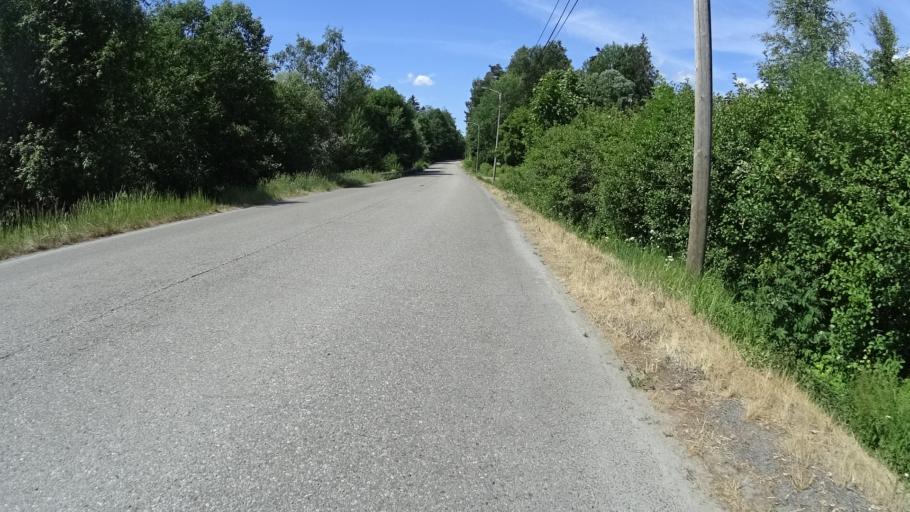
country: FI
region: Uusimaa
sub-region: Raaseporin
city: Karis
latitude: 60.0950
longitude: 23.5977
